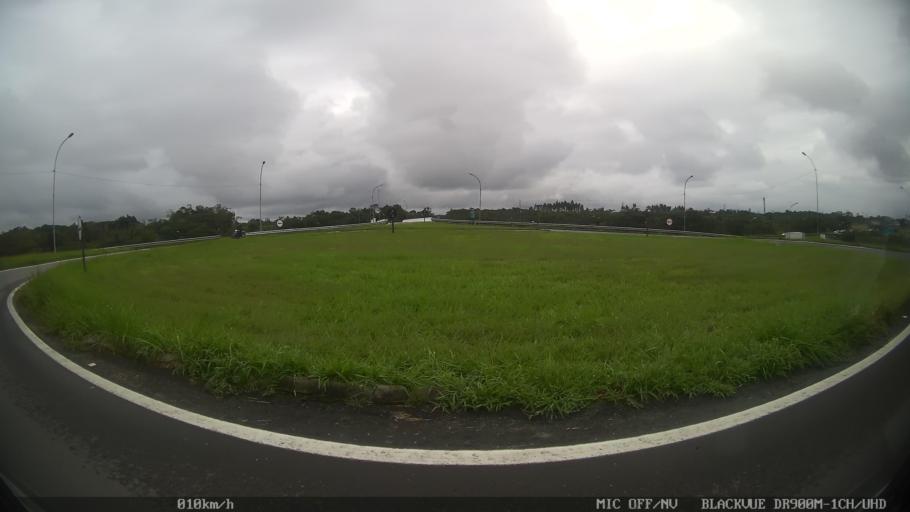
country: BR
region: Sao Paulo
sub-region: Registro
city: Registro
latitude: -24.5394
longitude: -47.8590
